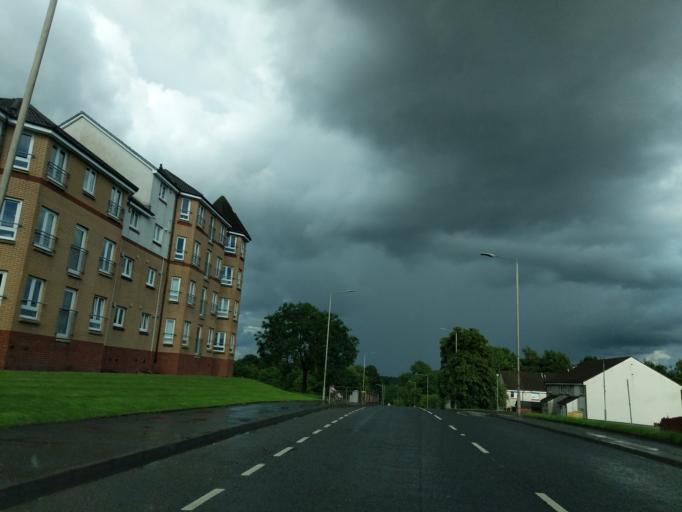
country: GB
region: Scotland
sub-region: East Renfrewshire
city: Newton Mearns
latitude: 55.8077
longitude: -4.3523
